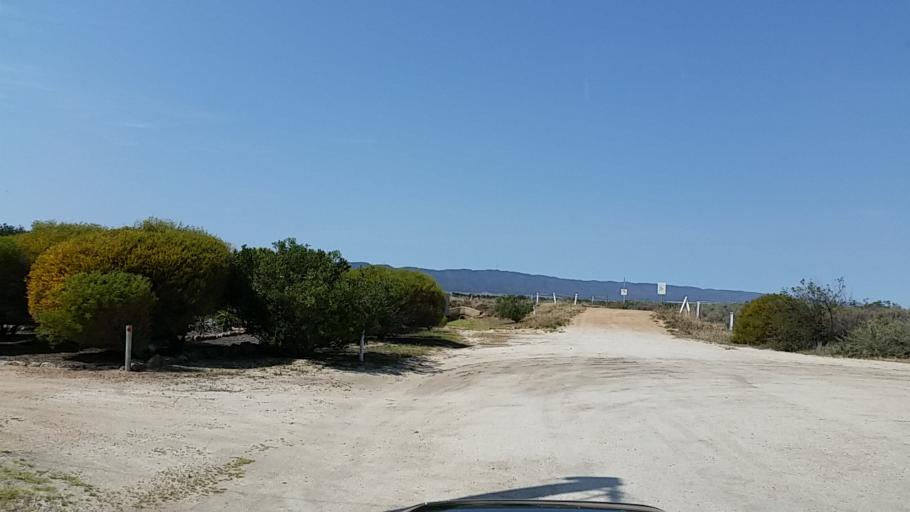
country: AU
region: South Australia
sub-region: Port Pirie City and Dists
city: Port Pirie
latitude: -33.0257
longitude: 138.0051
